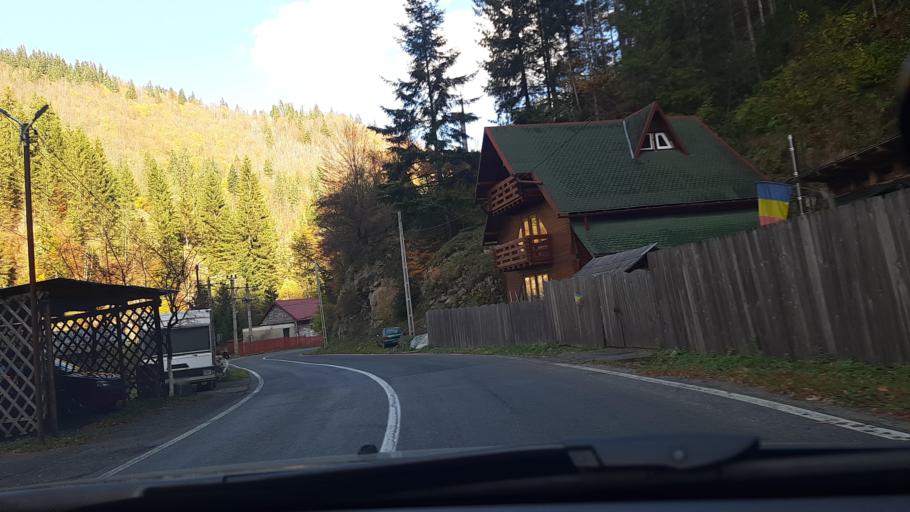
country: RO
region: Valcea
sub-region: Comuna Voineasa
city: Voineasa
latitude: 45.4243
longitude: 23.9455
